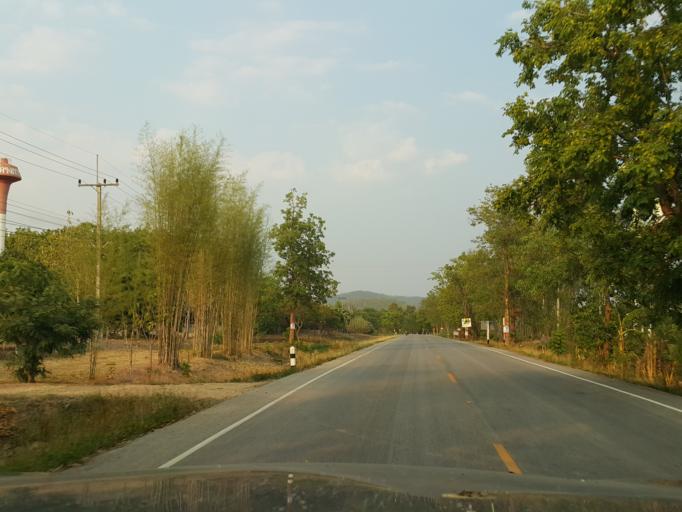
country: TH
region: Lamphun
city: Li
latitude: 17.8174
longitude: 98.9681
